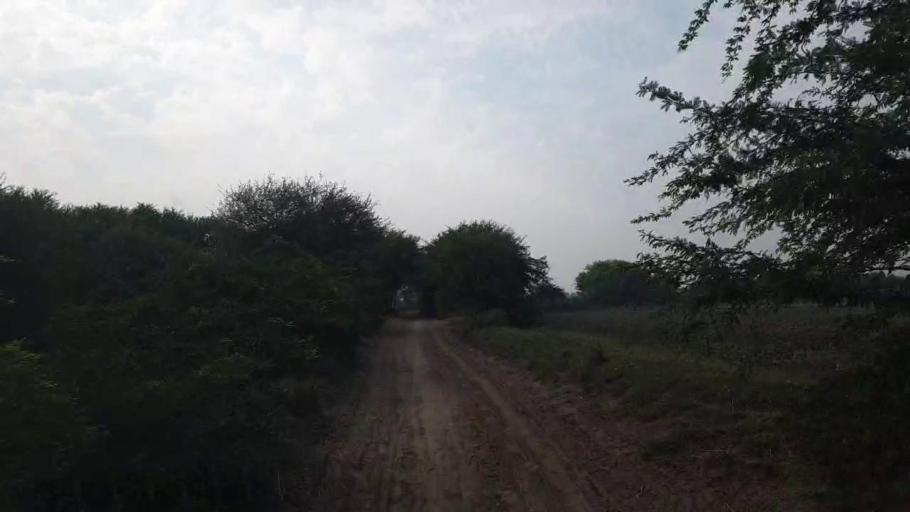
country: PK
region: Sindh
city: Tando Bago
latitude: 24.7851
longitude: 68.8799
